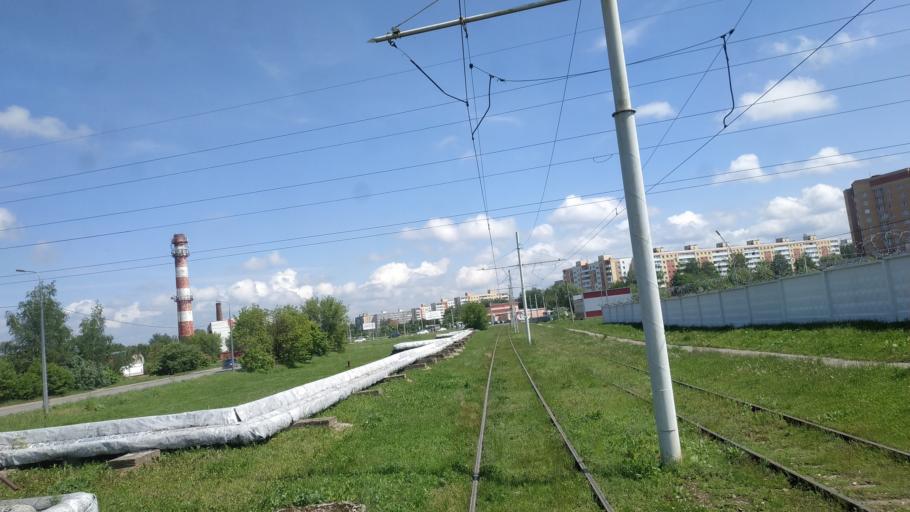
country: RU
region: Moskovskaya
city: Sychevo
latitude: 55.0607
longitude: 38.7369
